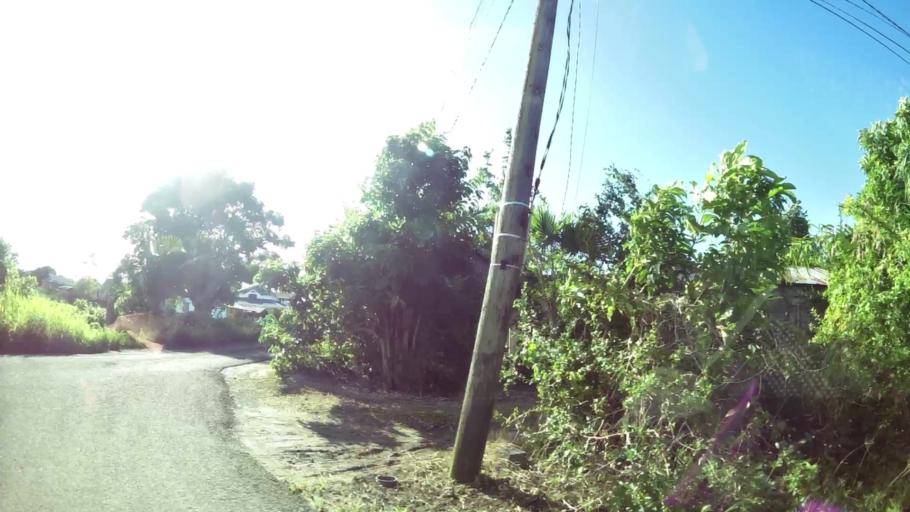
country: GP
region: Guadeloupe
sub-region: Guadeloupe
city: Le Moule
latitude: 16.3165
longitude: -61.4275
